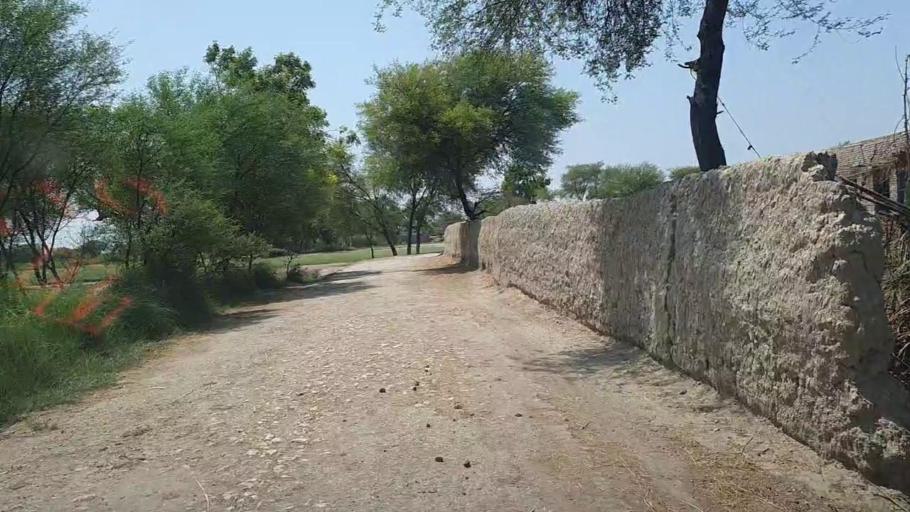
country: PK
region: Sindh
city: Ubauro
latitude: 28.1984
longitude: 69.8027
